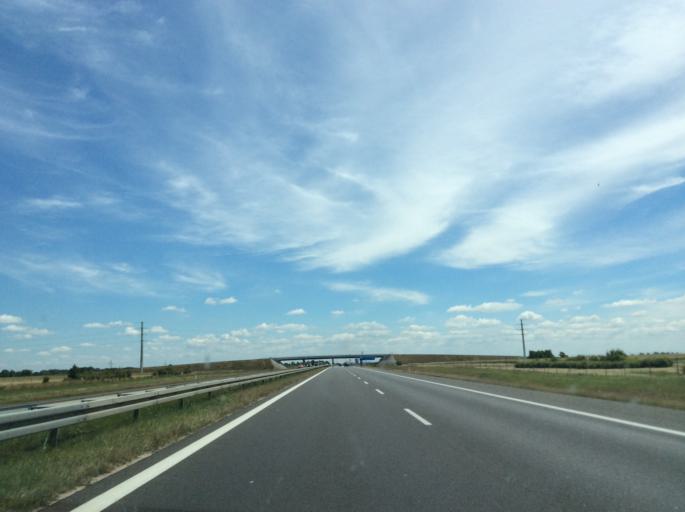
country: PL
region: Greater Poland Voivodeship
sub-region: Powiat poznanski
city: Swarzedz
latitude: 52.3330
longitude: 17.0733
